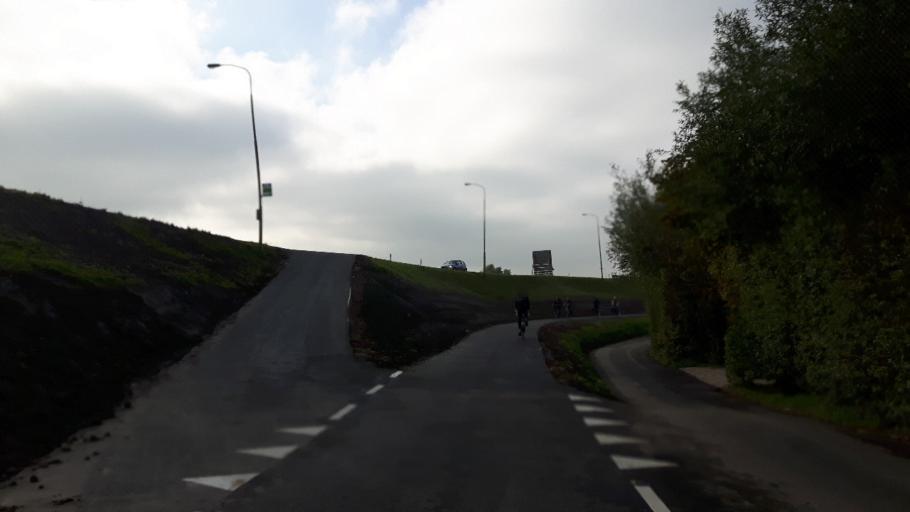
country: NL
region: South Holland
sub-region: Gemeente Gouda
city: Gouda
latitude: 51.9945
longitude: 4.6840
